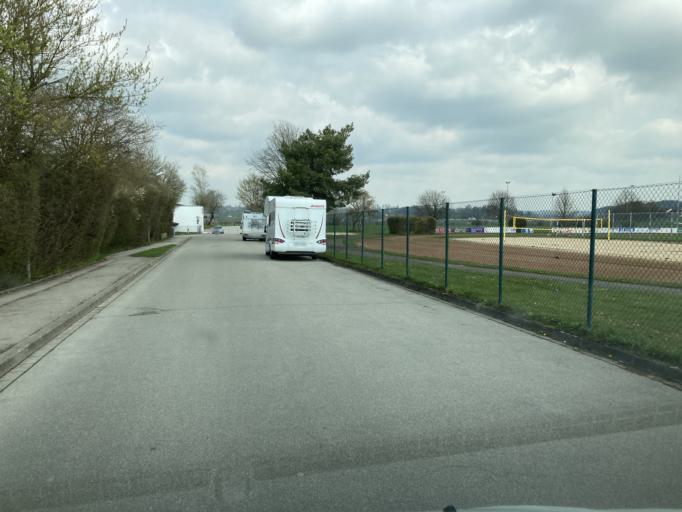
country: DE
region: Bavaria
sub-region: Upper Bavaria
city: Grafing bei Munchen
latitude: 48.0502
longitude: 11.9702
